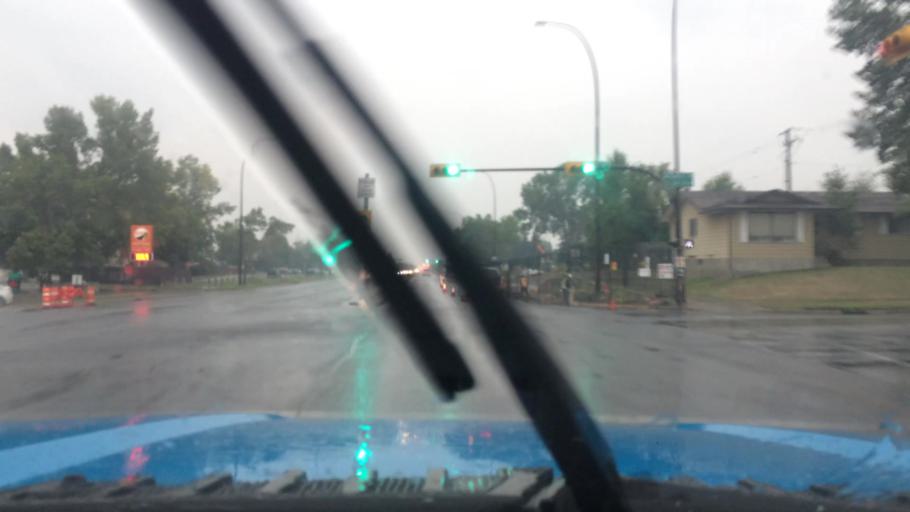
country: CA
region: Alberta
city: Calgary
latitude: 51.0917
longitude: -113.9586
